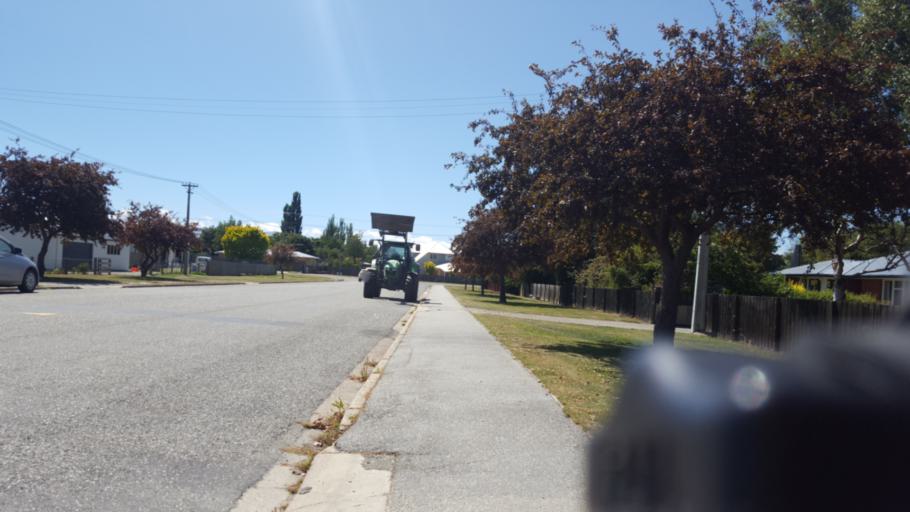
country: NZ
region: Otago
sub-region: Dunedin City
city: Dunedin
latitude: -45.1281
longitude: 170.1047
